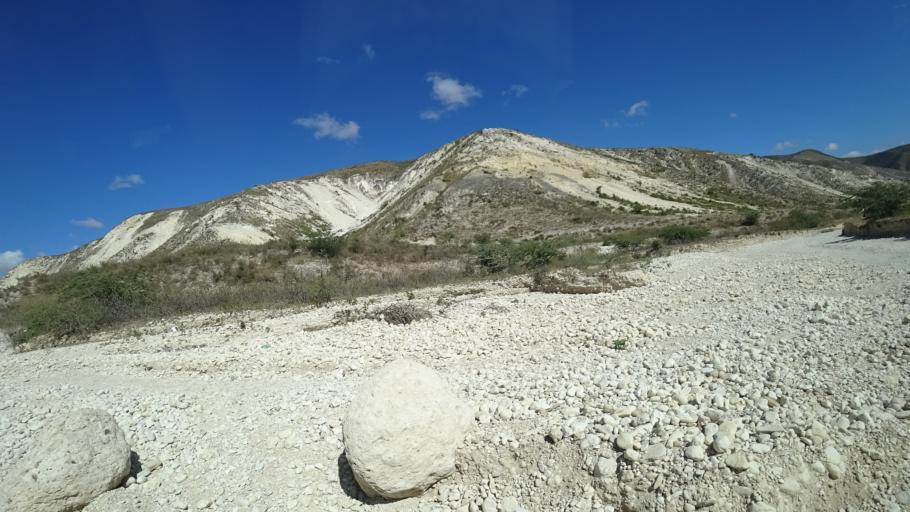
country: HT
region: Ouest
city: Croix des Bouquets
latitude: 18.6752
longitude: -72.2532
